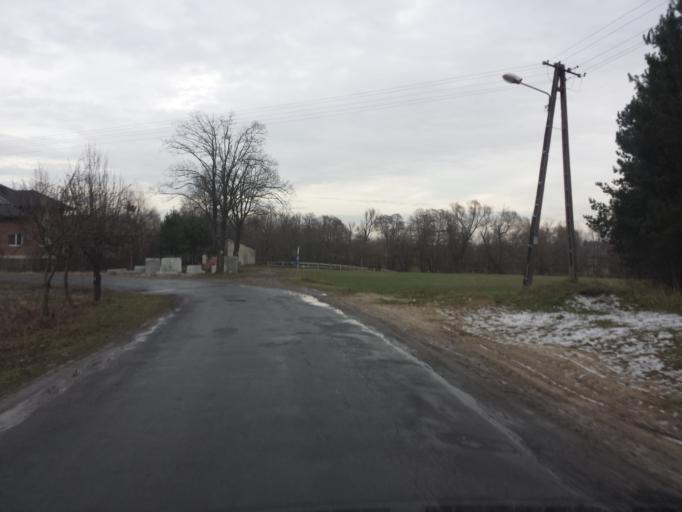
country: PL
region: Lodz Voivodeship
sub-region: Powiat wielunski
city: Osjakow
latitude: 51.2852
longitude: 18.7793
